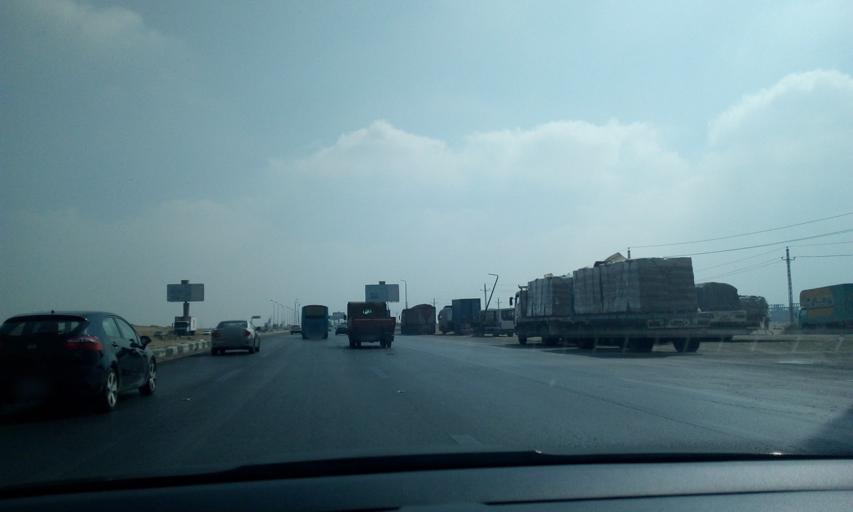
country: EG
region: Eastern Province
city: Bilbays
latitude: 30.2265
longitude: 31.6994
